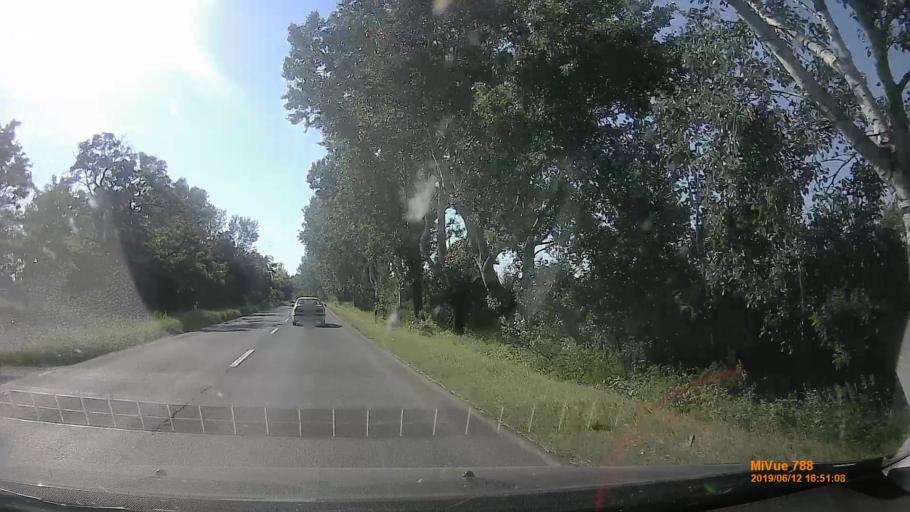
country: HU
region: Csongrad
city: Kiszombor
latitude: 46.2053
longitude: 20.3822
